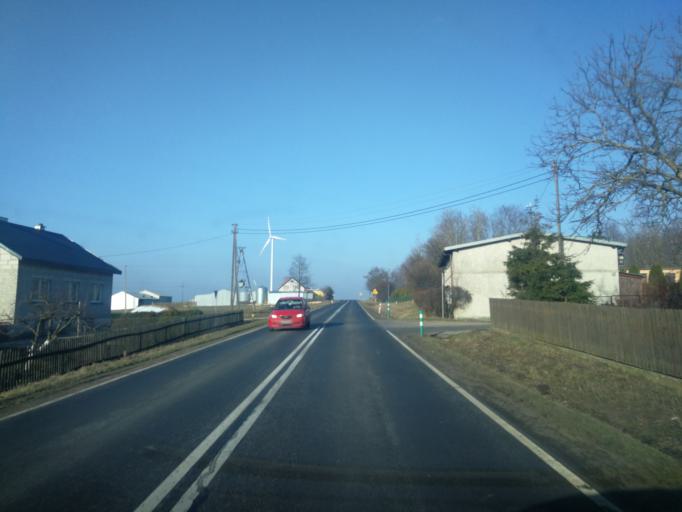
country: PL
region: Warmian-Masurian Voivodeship
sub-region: Powiat ilawski
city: Lubawa
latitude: 53.5491
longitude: 19.7622
